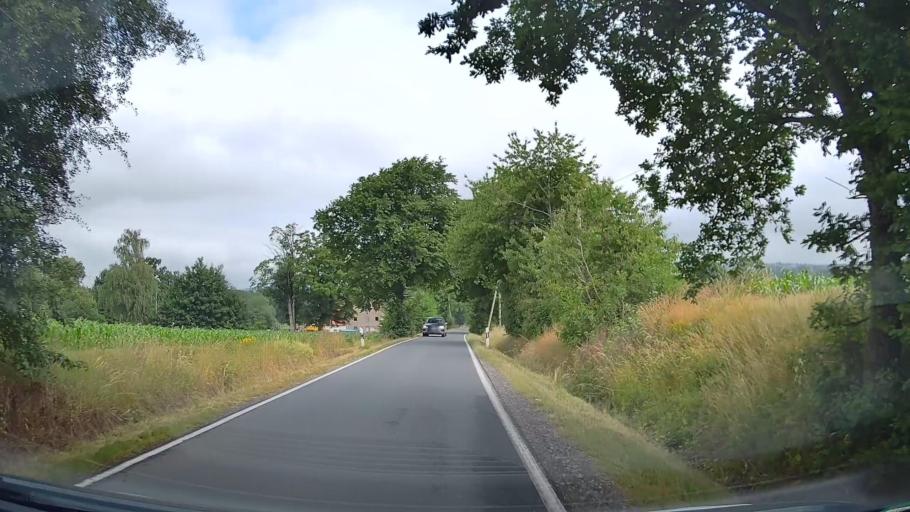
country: DE
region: North Rhine-Westphalia
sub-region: Regierungsbezirk Detmold
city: Barntrup
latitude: 52.0863
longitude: 9.1328
